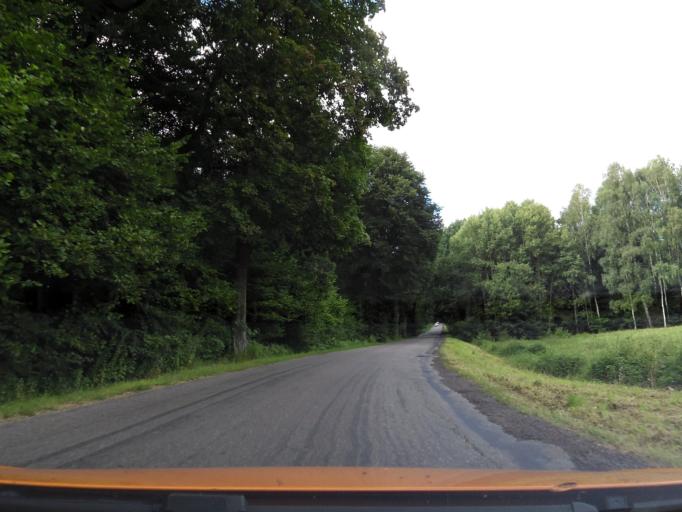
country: PL
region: West Pomeranian Voivodeship
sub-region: Powiat kolobrzeski
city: Ryman
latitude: 53.9540
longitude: 15.4942
